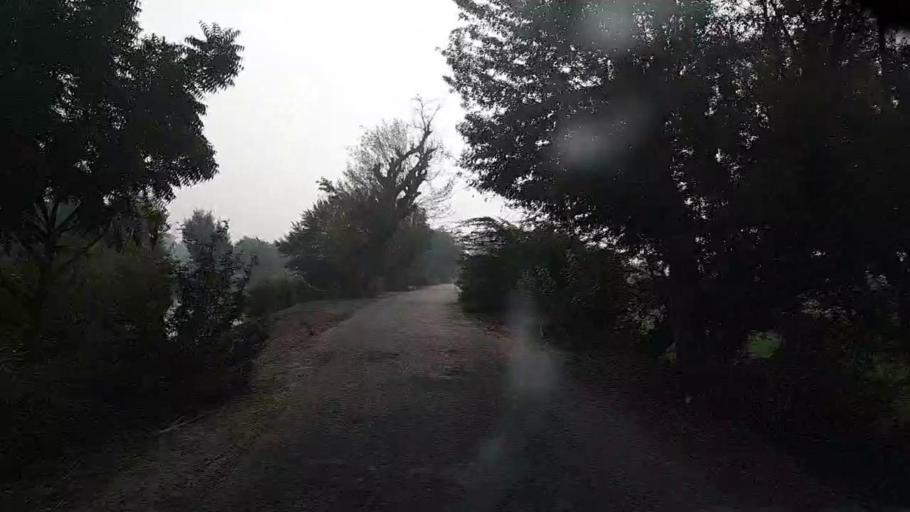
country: PK
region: Sindh
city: Bozdar
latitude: 27.1396
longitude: 68.6550
